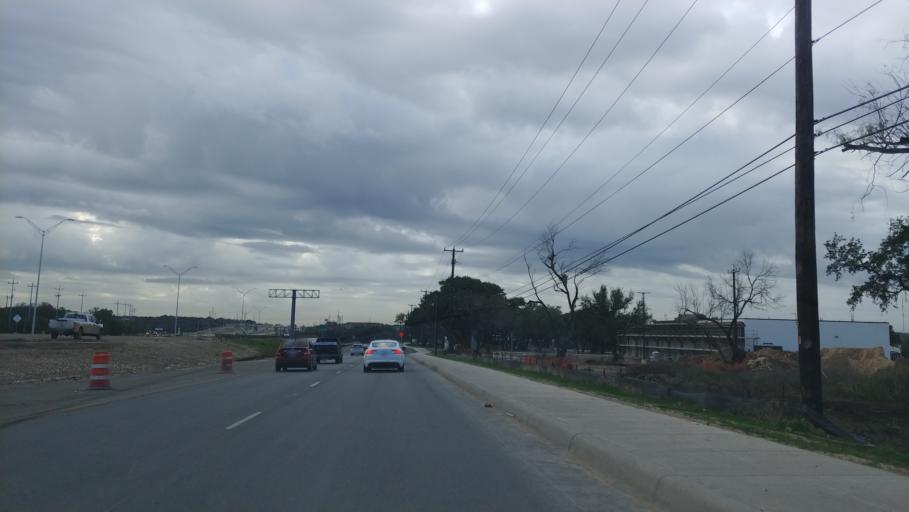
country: US
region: Texas
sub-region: Bexar County
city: Lackland Air Force Base
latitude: 29.4292
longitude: -98.7118
